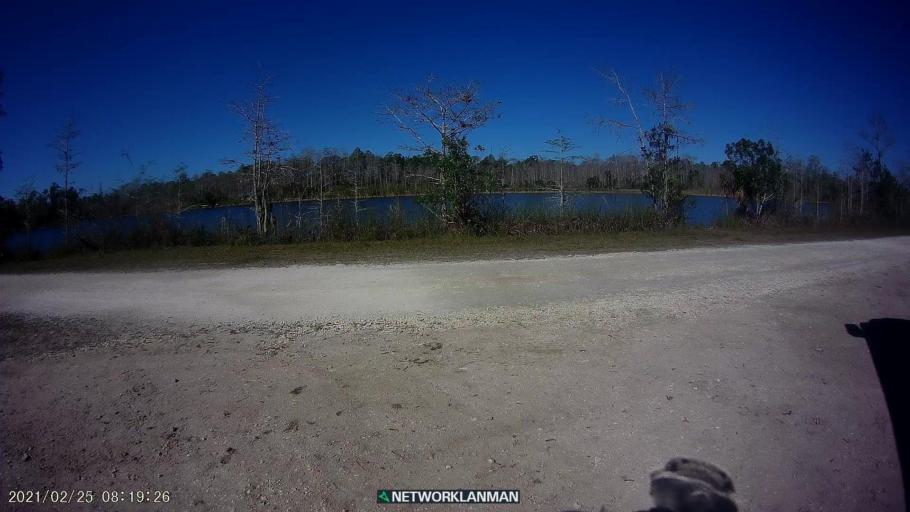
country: US
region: Florida
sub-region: Collier County
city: Lely Resort
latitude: 25.8926
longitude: -81.2299
